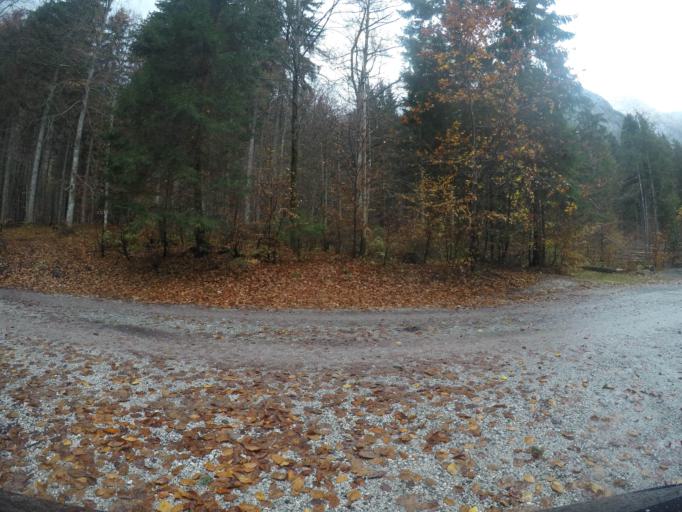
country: SI
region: Kranjska Gora
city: Mojstrana
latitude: 46.4122
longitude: 13.8460
